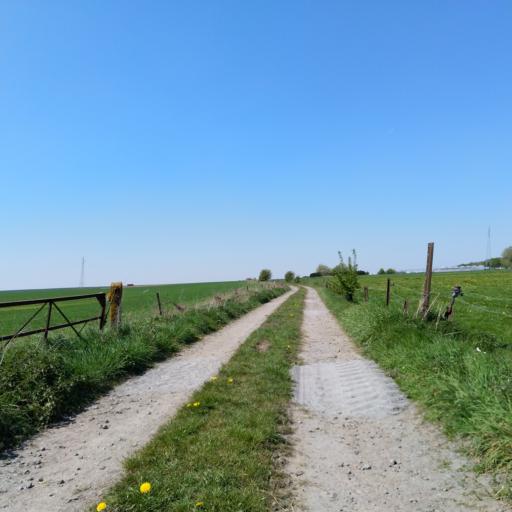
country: BE
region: Wallonia
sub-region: Province du Hainaut
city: Lens
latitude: 50.5598
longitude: 3.8932
